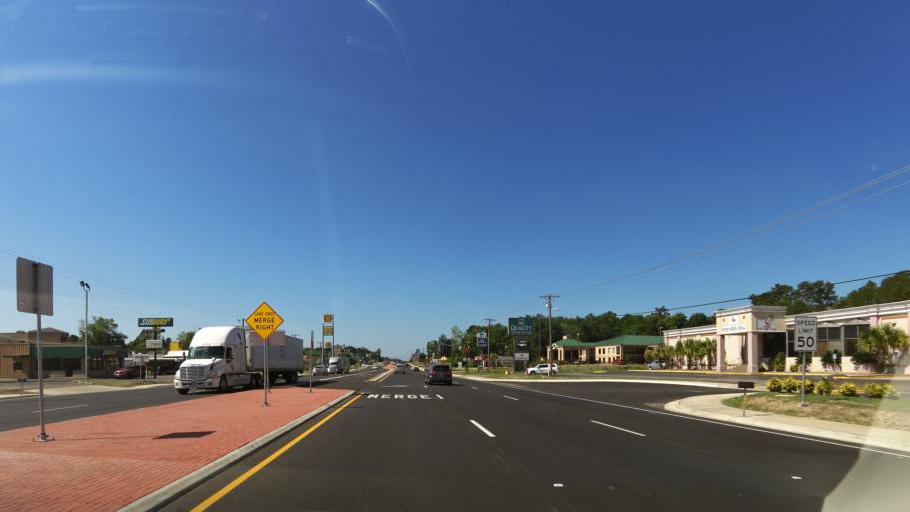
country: US
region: Texas
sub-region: Nacogdoches County
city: Nacogdoches
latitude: 31.5749
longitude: -94.6732
